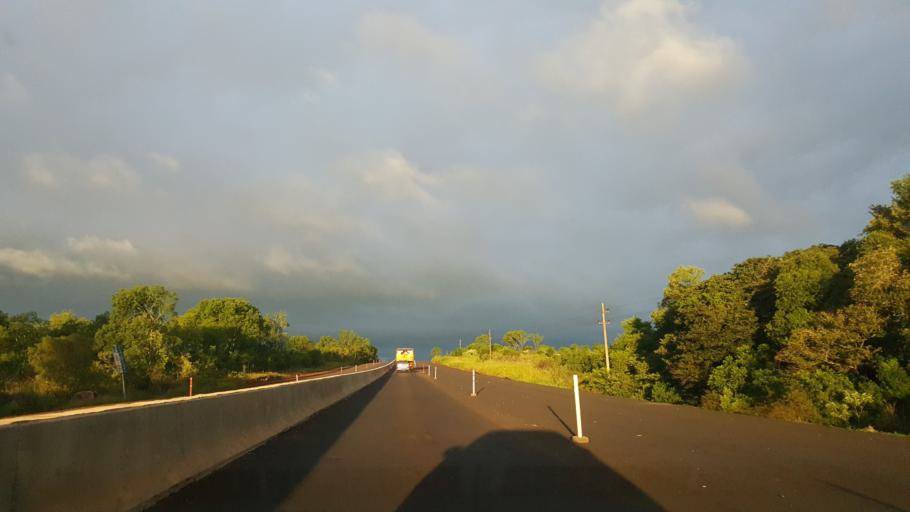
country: AR
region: Misiones
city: Santa Ana
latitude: -27.4258
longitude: -55.6246
